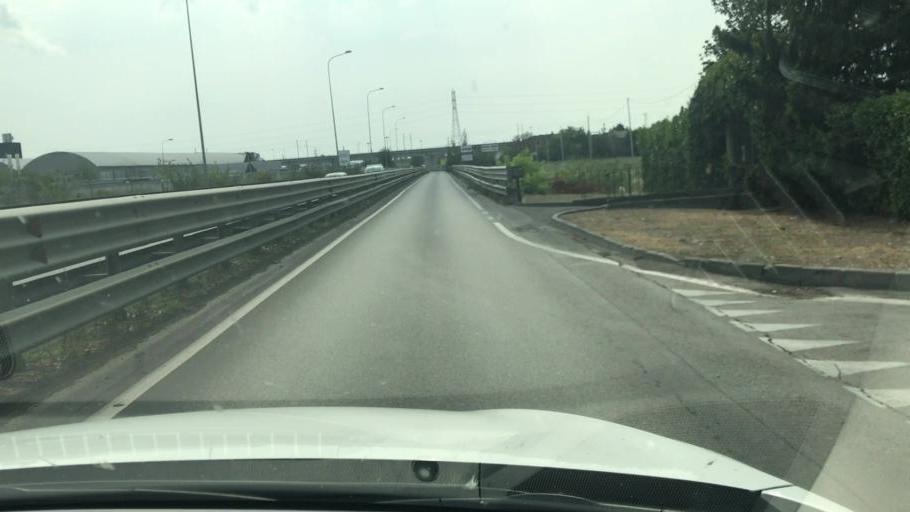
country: IT
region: Emilia-Romagna
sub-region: Provincia di Parma
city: Baganzola
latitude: 44.8454
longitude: 10.3407
